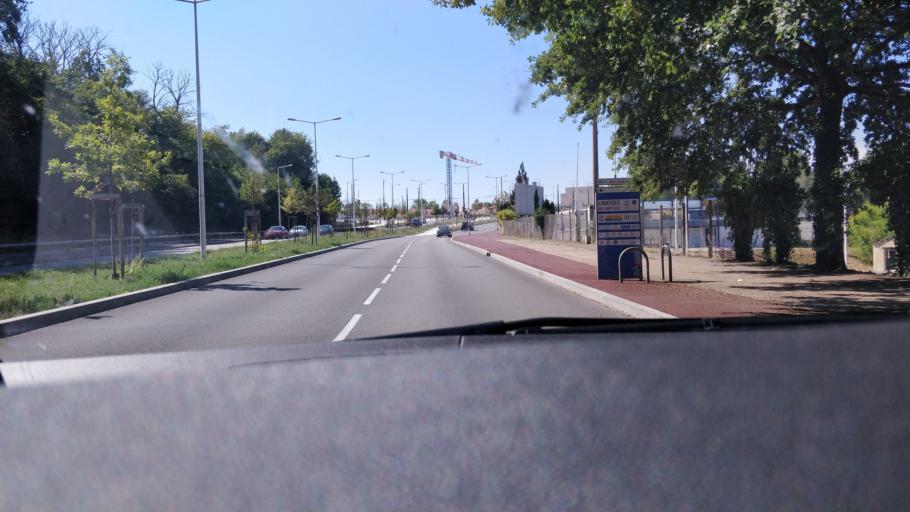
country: FR
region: Limousin
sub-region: Departement de la Haute-Vienne
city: Limoges
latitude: 45.8585
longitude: 1.2709
